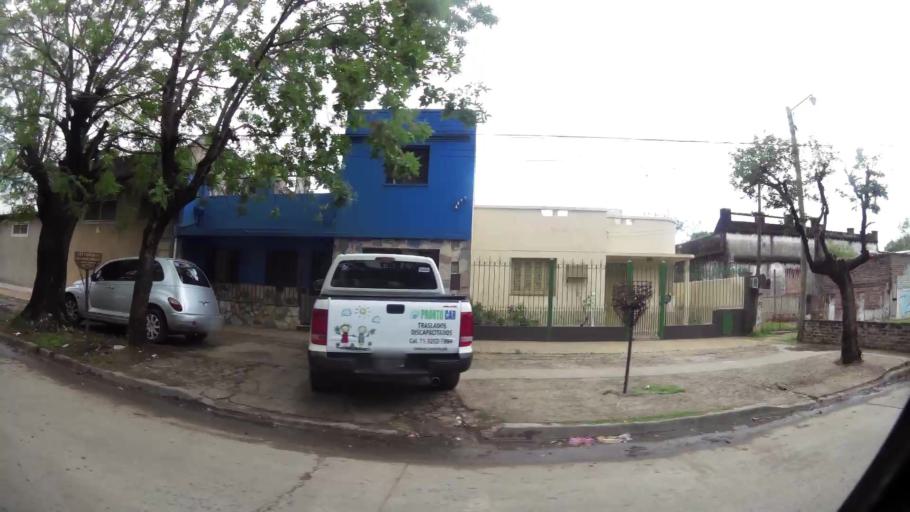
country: AR
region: Buenos Aires
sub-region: Partido de Lomas de Zamora
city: Lomas de Zamora
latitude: -34.7374
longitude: -58.3819
